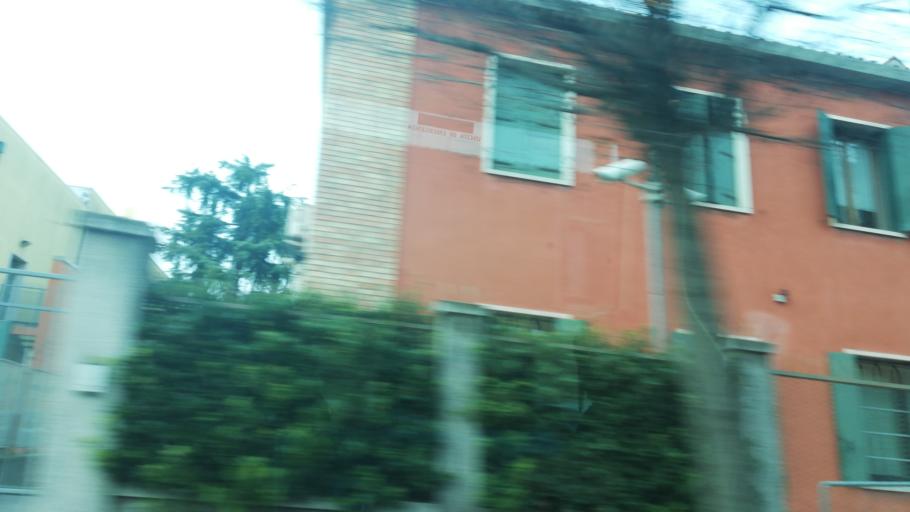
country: IT
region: Veneto
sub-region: Provincia di Venezia
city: Mestre
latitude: 45.4971
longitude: 12.2492
